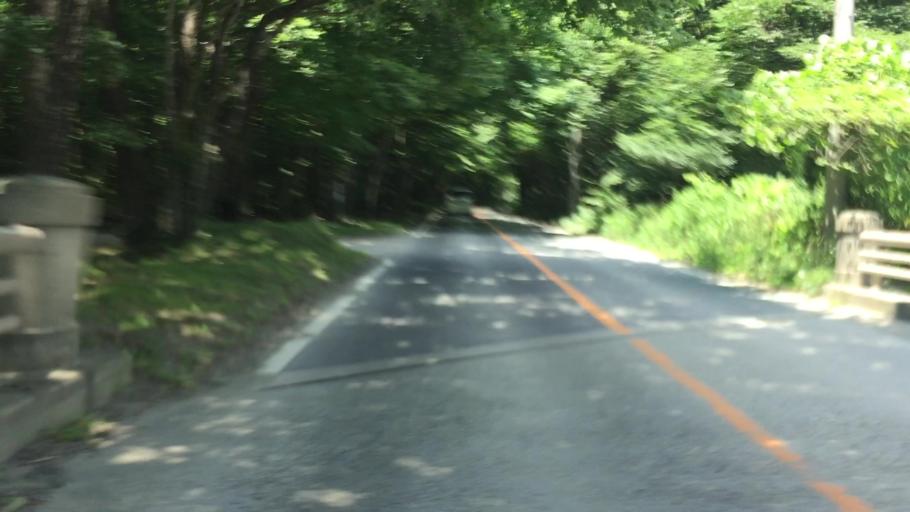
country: JP
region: Tochigi
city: Kuroiso
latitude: 37.0228
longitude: 140.0065
